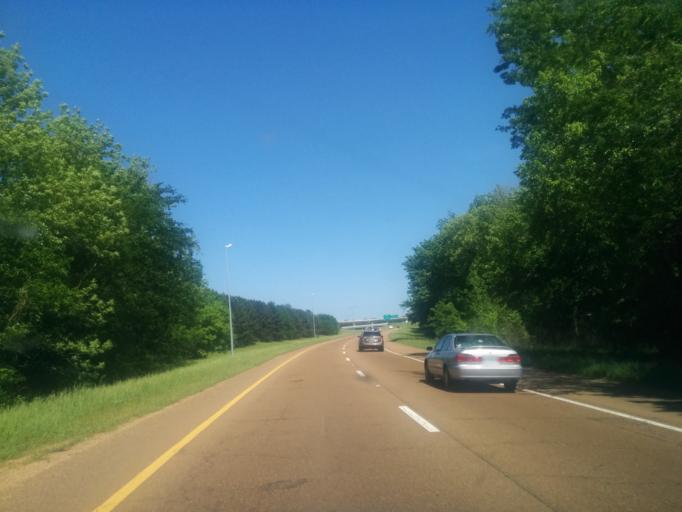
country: US
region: Mississippi
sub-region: Madison County
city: Ridgeland
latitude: 32.4125
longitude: -90.1566
